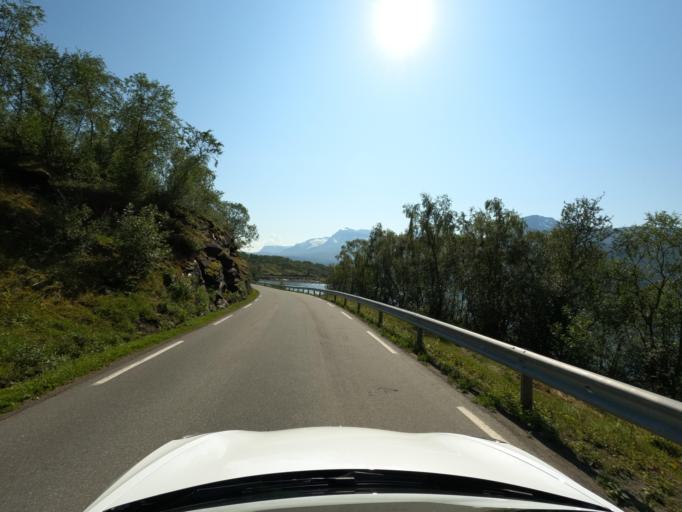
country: NO
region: Nordland
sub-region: Narvik
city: Narvik
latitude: 68.3413
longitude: 17.2772
